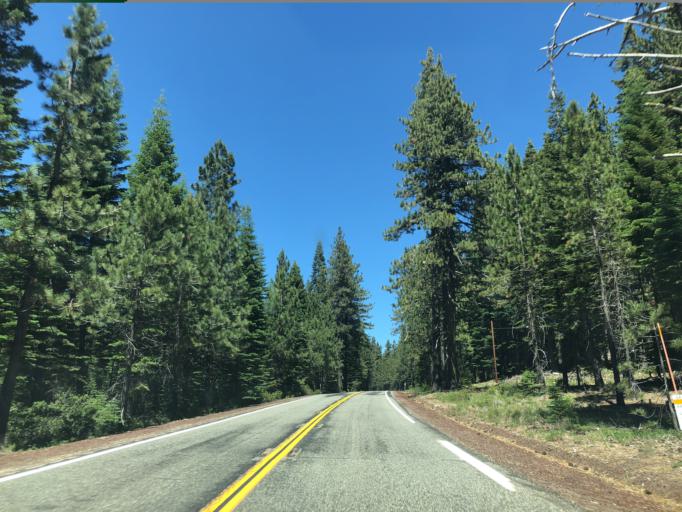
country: US
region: California
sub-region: Shasta County
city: Shingletown
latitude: 40.5547
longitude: -121.5797
